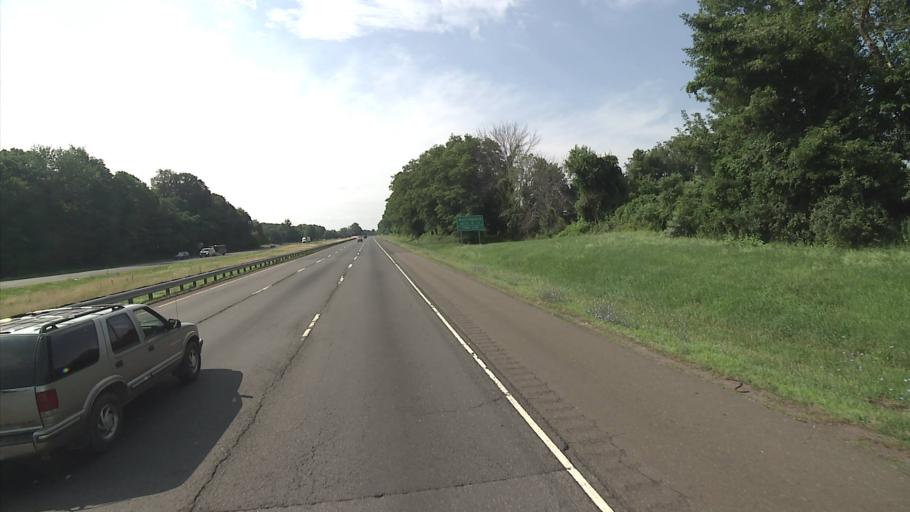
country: US
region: Connecticut
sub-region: New Haven County
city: Meriden
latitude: 41.4973
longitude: -72.7686
